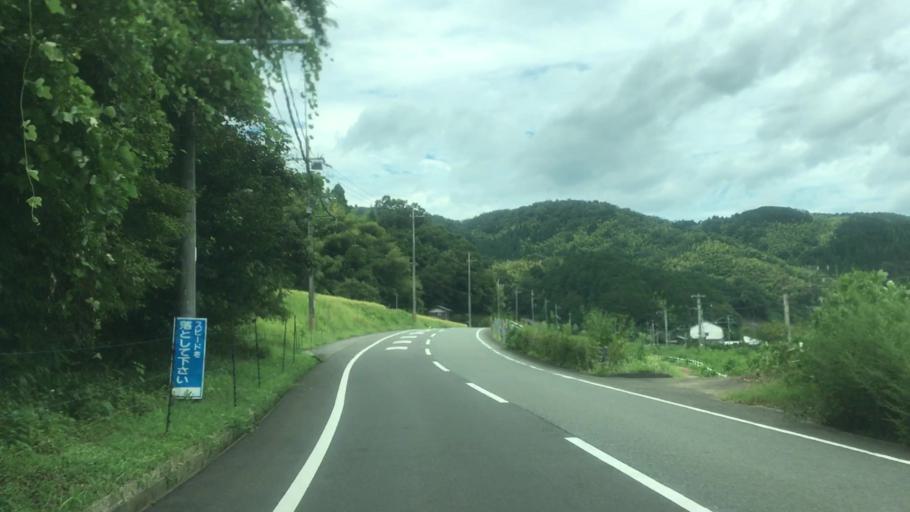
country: JP
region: Hyogo
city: Toyooka
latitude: 35.5761
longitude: 134.8035
